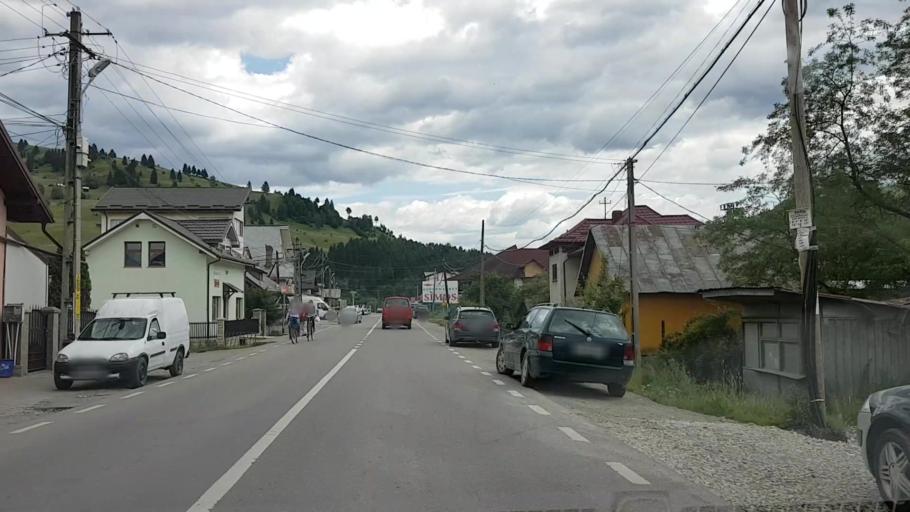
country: RO
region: Neamt
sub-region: Comuna Borca
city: Borca
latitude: 47.1802
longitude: 25.7840
